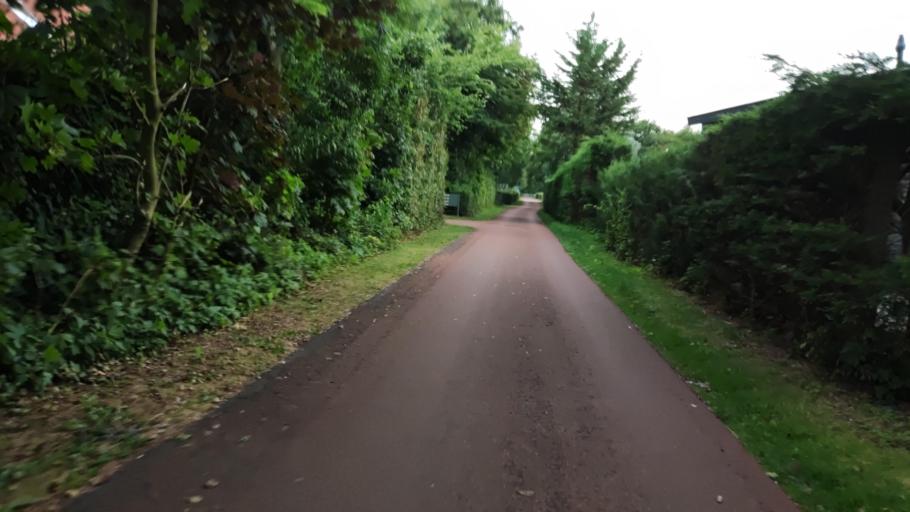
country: NL
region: North Holland
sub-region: Gemeente Texel
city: Den Burg
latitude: 53.0871
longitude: 4.7697
